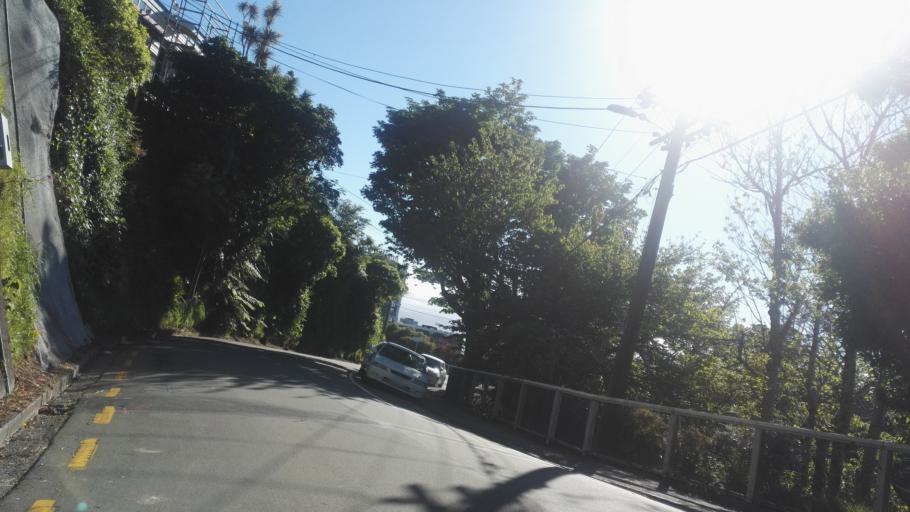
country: NZ
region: Wellington
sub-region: Wellington City
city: Kelburn
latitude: -41.2918
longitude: 174.7658
